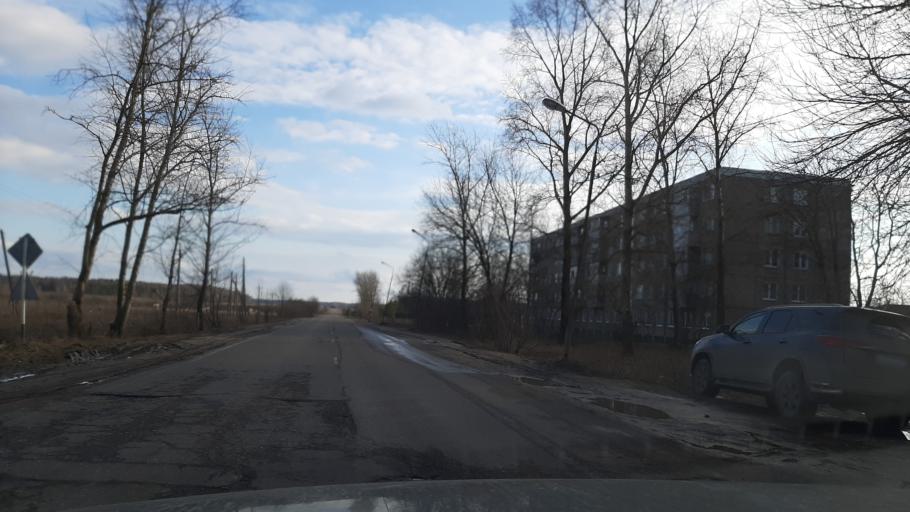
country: RU
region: Ivanovo
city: Novo-Talitsy
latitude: 56.9230
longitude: 40.7387
